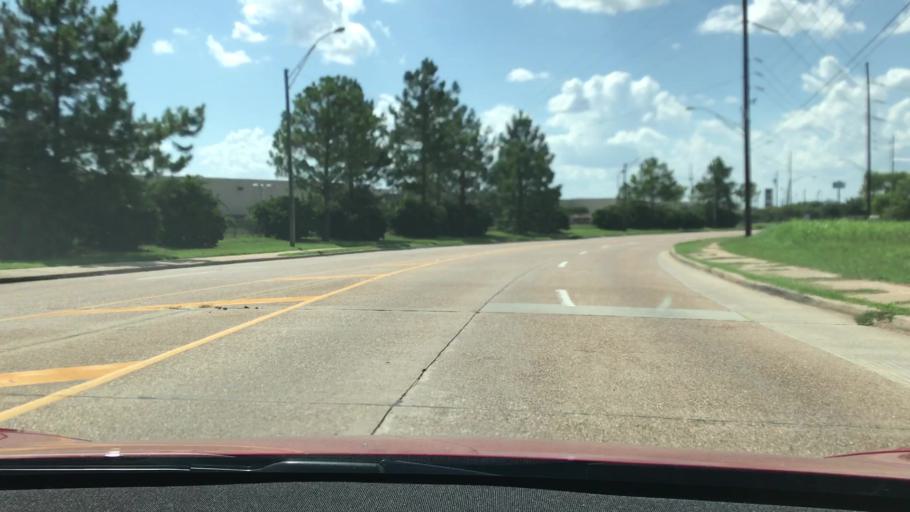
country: US
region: Louisiana
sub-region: Bossier Parish
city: Bossier City
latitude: 32.4411
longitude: -93.7122
